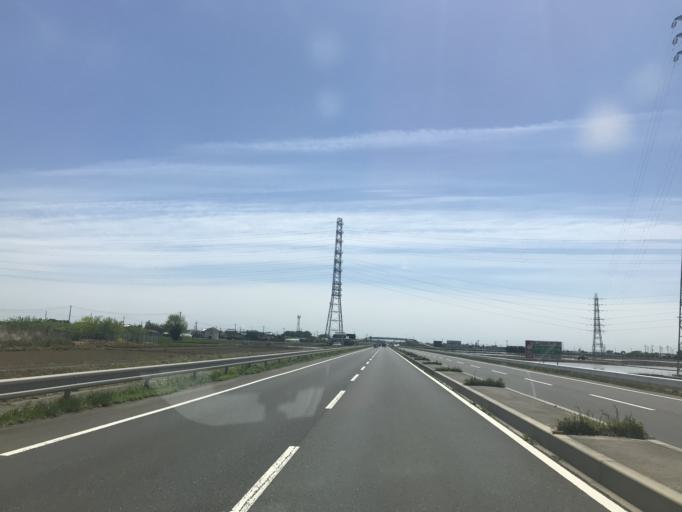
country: JP
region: Ibaraki
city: Ishige
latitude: 36.1777
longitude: 139.9908
